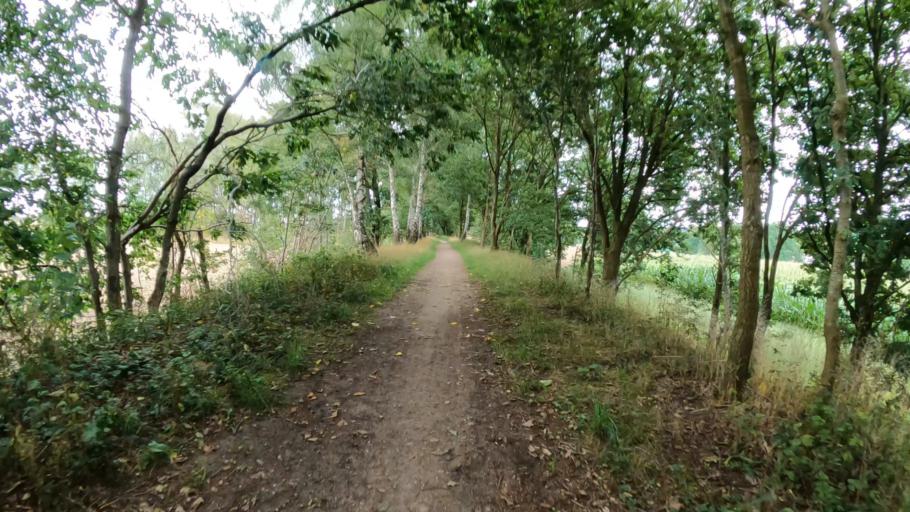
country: DE
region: Lower Saxony
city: Kakenstorf
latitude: 53.3115
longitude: 9.7973
